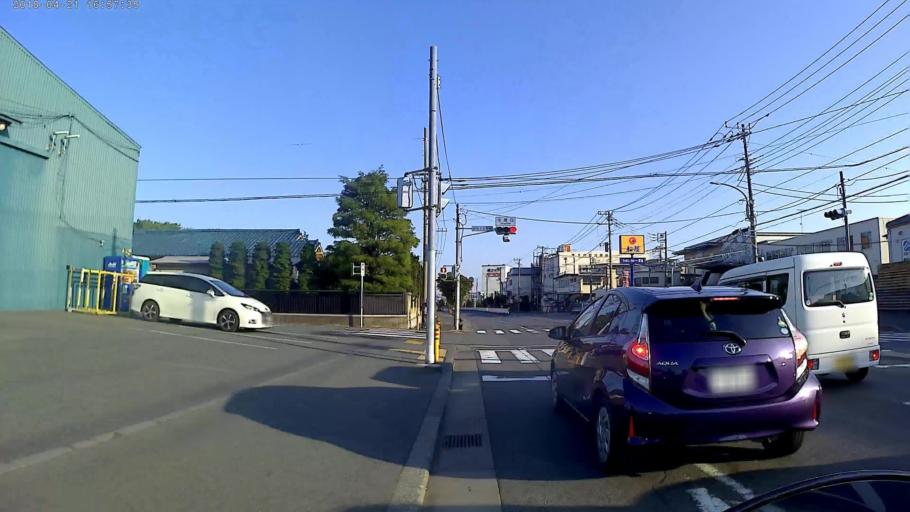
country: JP
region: Kanagawa
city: Minami-rinkan
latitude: 35.4528
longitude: 139.4180
